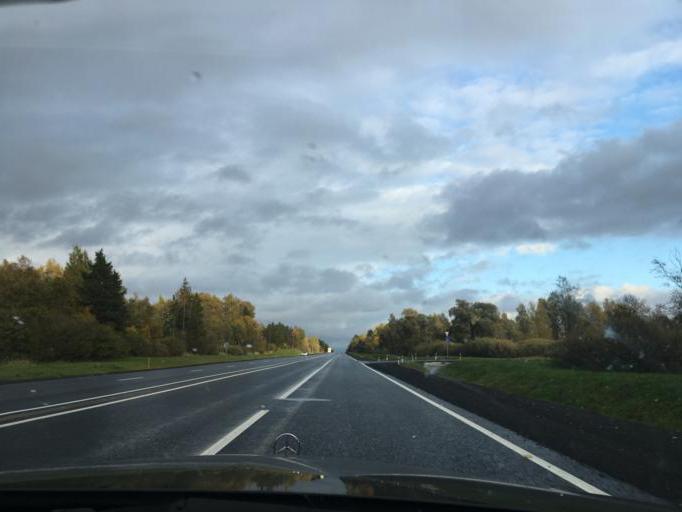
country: RU
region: Smolensk
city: Katyn'
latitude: 54.8452
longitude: 31.6991
